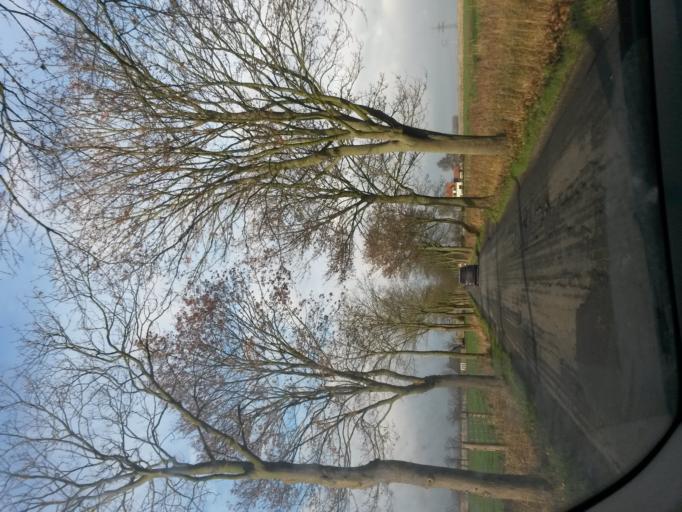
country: DE
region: Lower Saxony
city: Neuenkirchen
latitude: 53.1902
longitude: 8.4886
